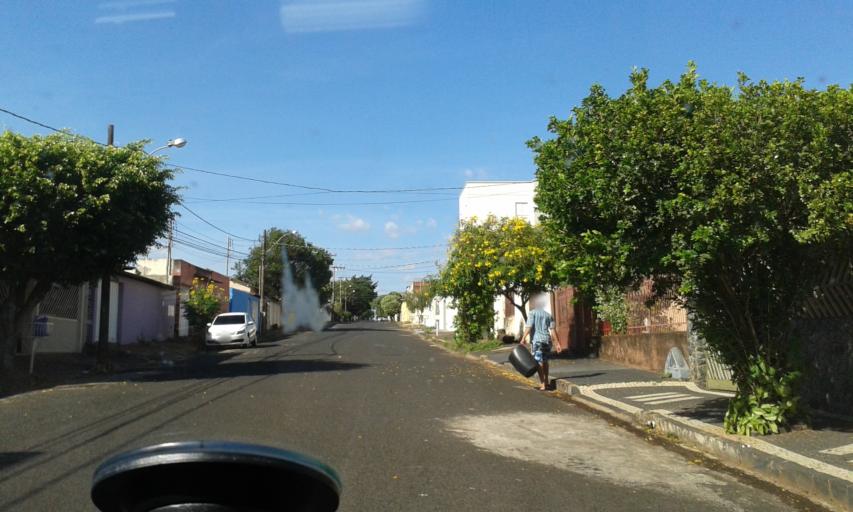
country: BR
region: Minas Gerais
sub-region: Uberlandia
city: Uberlandia
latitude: -18.9131
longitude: -48.2418
